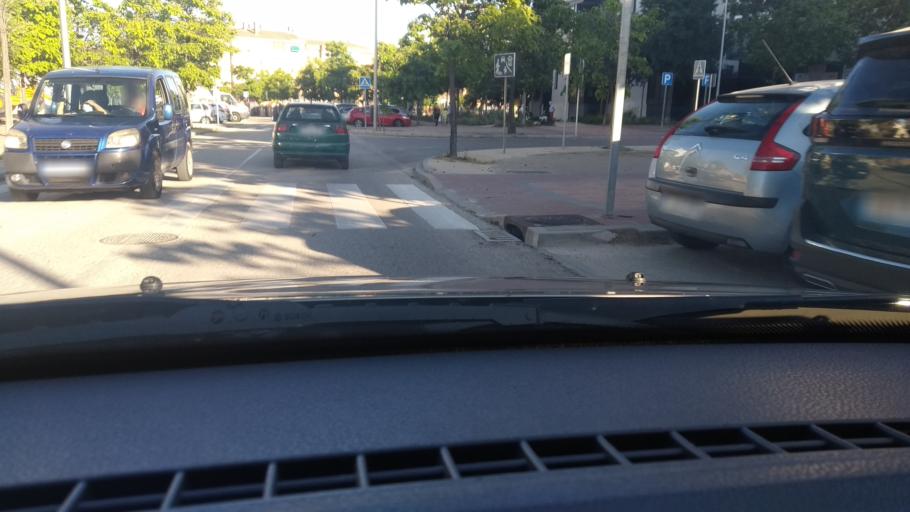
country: ES
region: Madrid
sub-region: Provincia de Madrid
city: Villa de Vallecas
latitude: 40.3766
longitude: -3.6257
